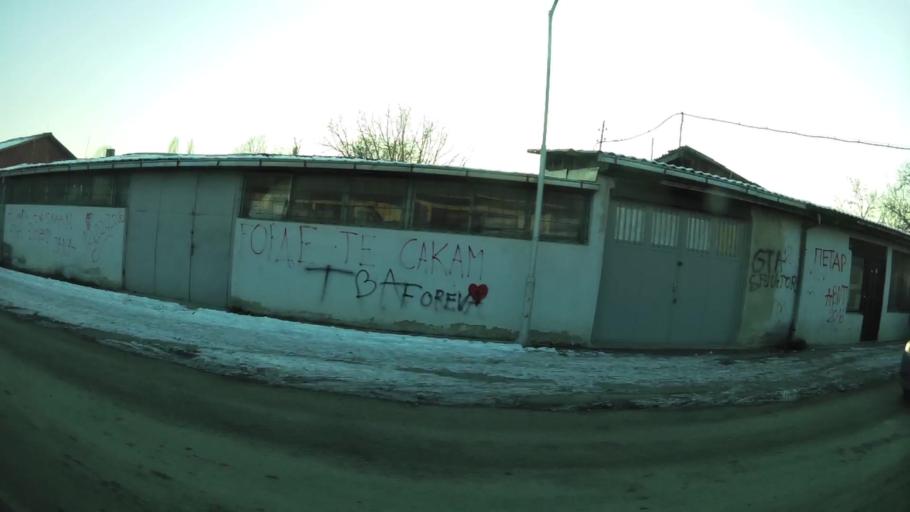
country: MK
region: Kisela Voda
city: Usje
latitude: 41.9724
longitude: 21.4796
